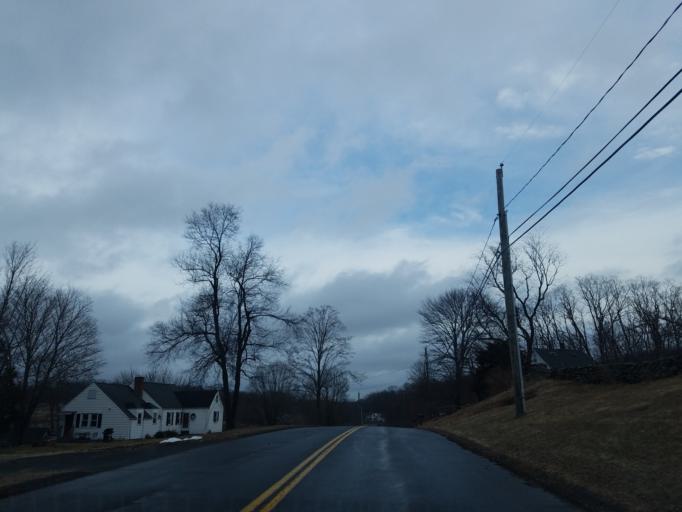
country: US
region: Connecticut
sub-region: Hartford County
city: Glastonbury Center
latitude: 41.6575
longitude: -72.5623
